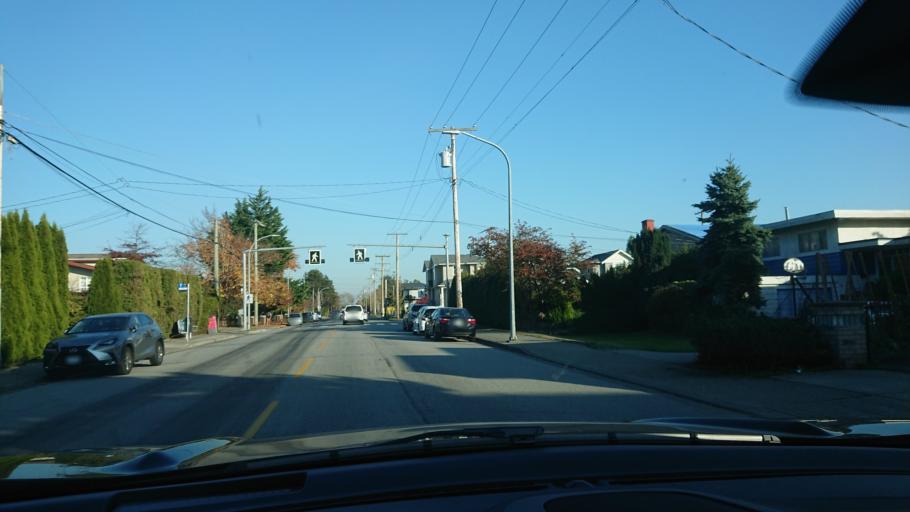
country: CA
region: British Columbia
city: Richmond
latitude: 49.1251
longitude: -123.1654
